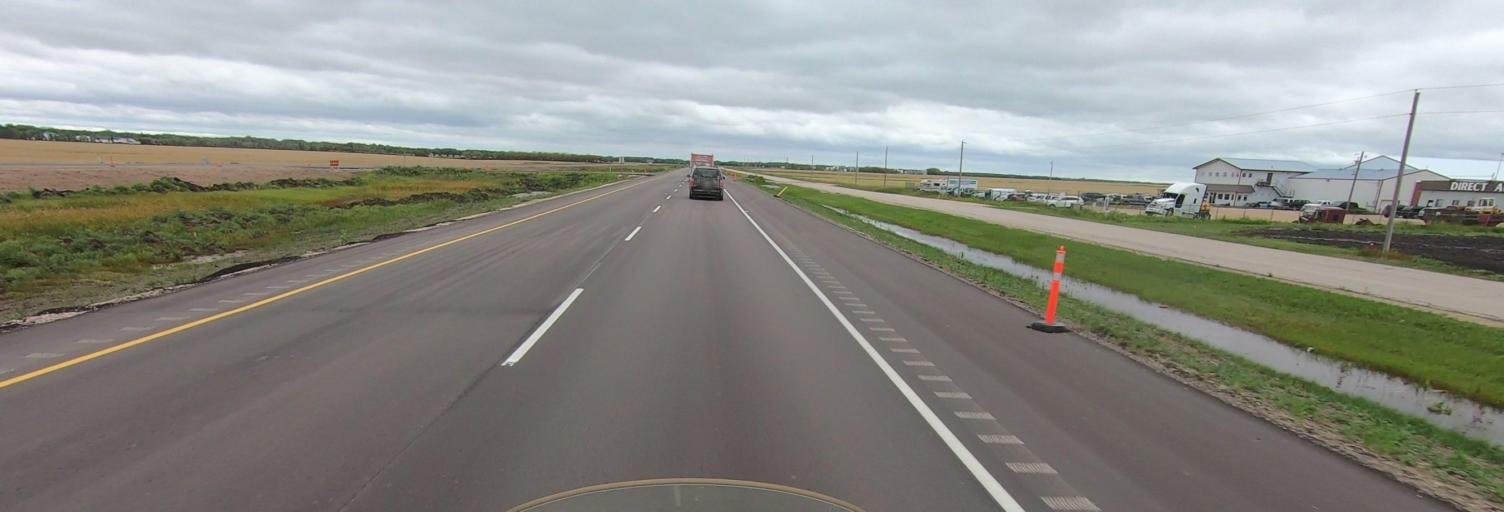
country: CA
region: Manitoba
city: Headingley
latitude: 49.8815
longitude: -97.4639
